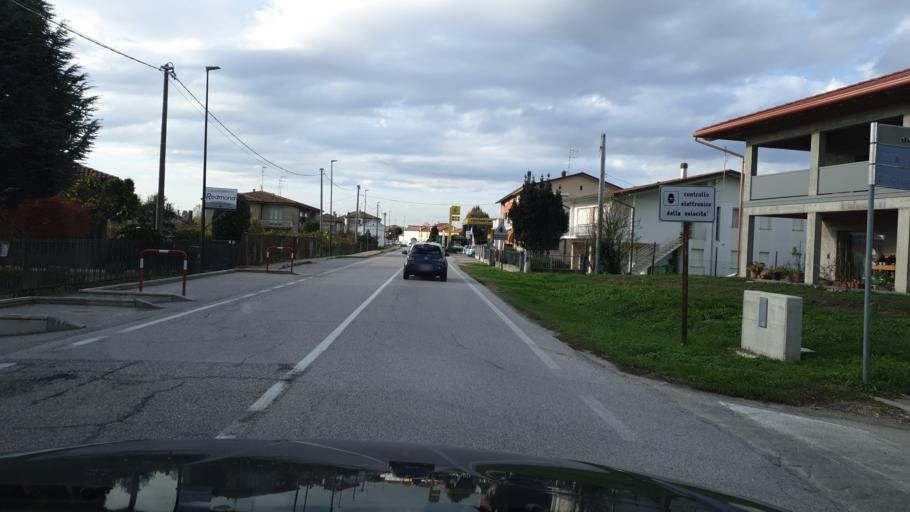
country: IT
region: Veneto
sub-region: Provincia di Rovigo
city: Villanova del Ghebbo Canton
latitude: 45.0590
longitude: 11.6394
